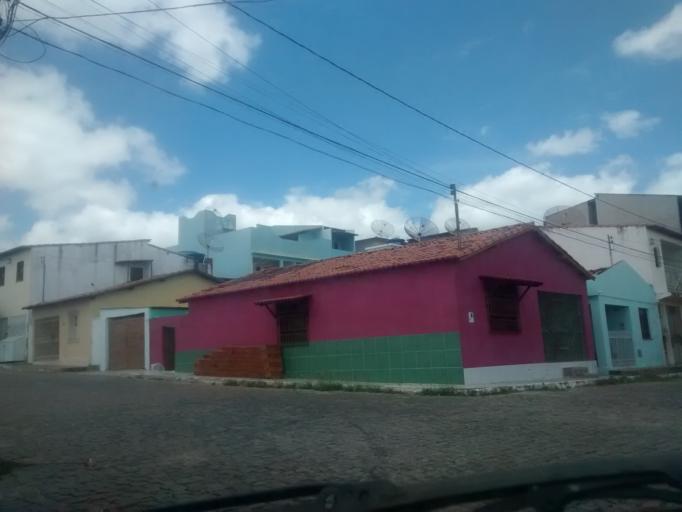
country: BR
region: Bahia
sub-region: Brumado
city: Brumado
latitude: -14.2020
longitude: -41.6734
